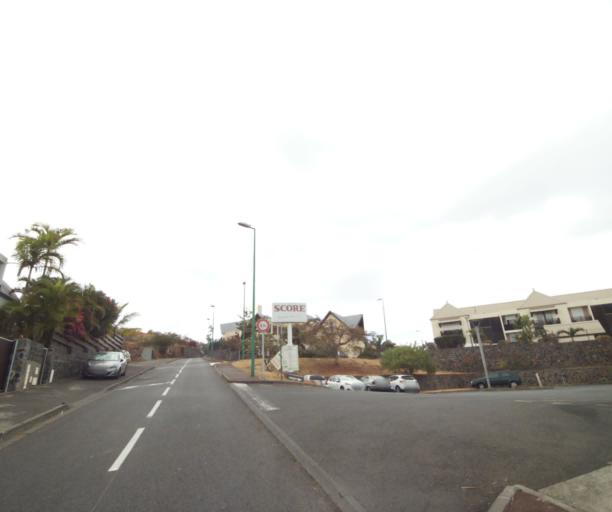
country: RE
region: Reunion
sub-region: Reunion
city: Saint-Paul
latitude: -21.0603
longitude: 55.2302
